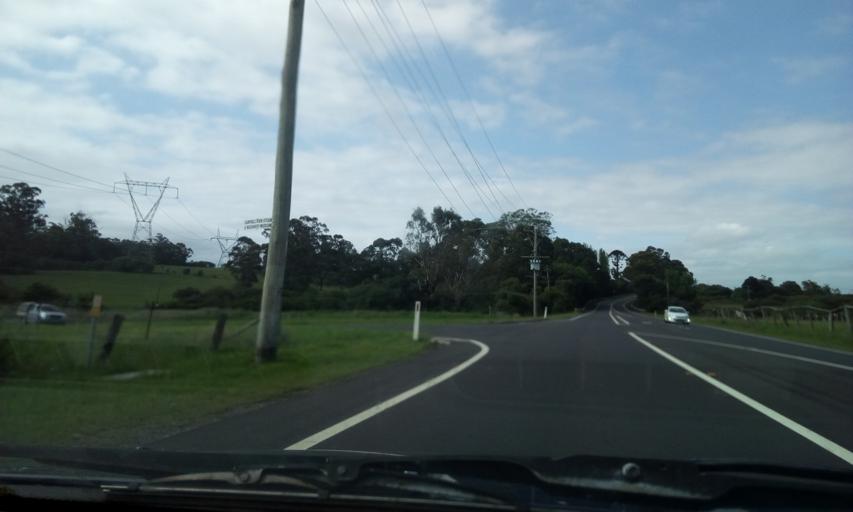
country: AU
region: New South Wales
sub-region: Campbelltown Municipality
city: Glen Alpine
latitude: -34.0938
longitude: 150.7702
